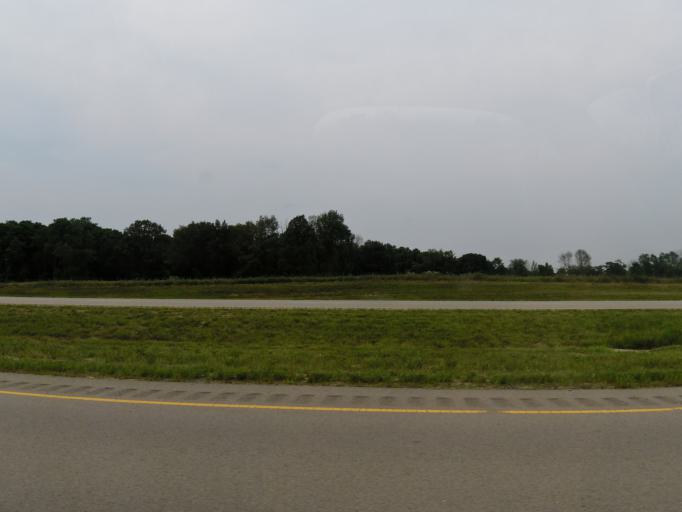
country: US
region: Ohio
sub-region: Clinton County
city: Wilmington
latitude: 39.4641
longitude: -83.8579
